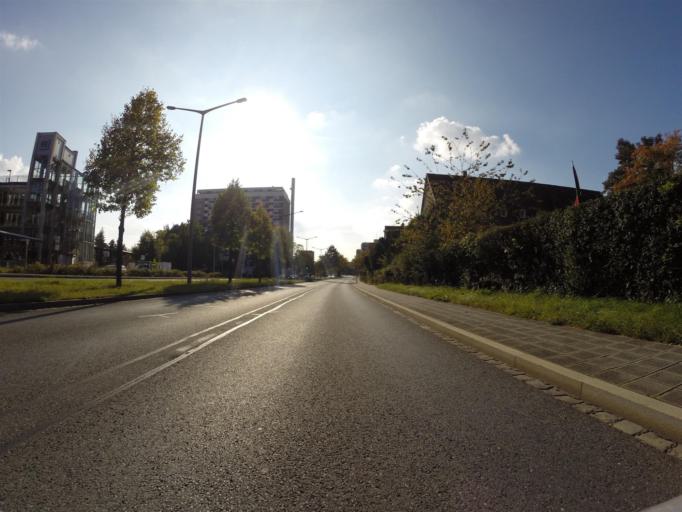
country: DE
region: Bavaria
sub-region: Regierungsbezirk Mittelfranken
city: Nuernberg
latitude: 49.4787
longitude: 11.1099
